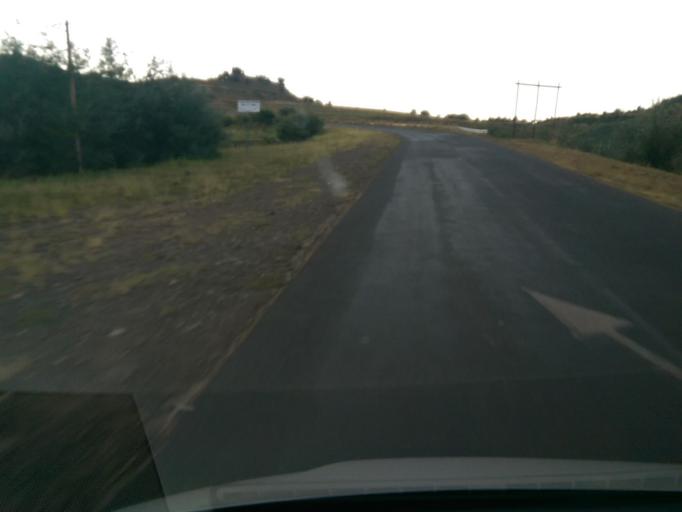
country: LS
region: Maseru
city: Nako
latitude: -29.4356
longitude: 27.6898
